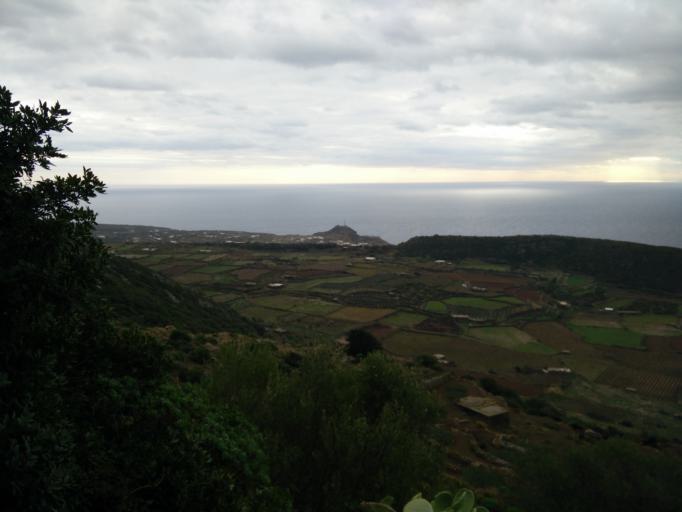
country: IT
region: Sicily
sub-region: Trapani
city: Kamma
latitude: 36.7766
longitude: 11.9851
